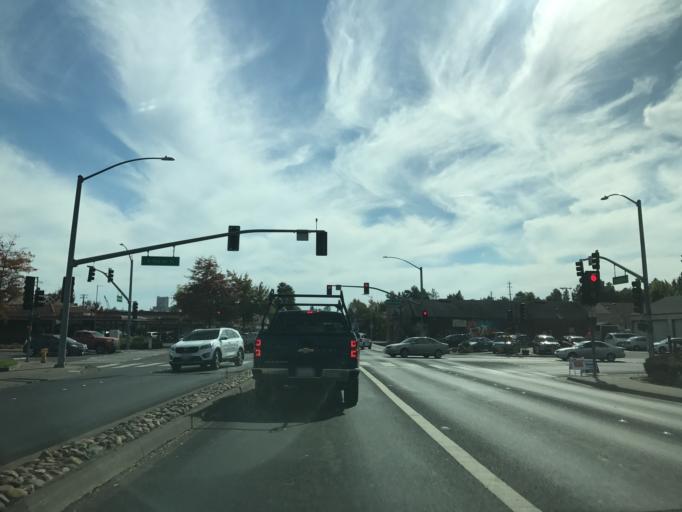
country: US
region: California
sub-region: Sonoma County
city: Petaluma
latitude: 38.2454
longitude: -122.6449
